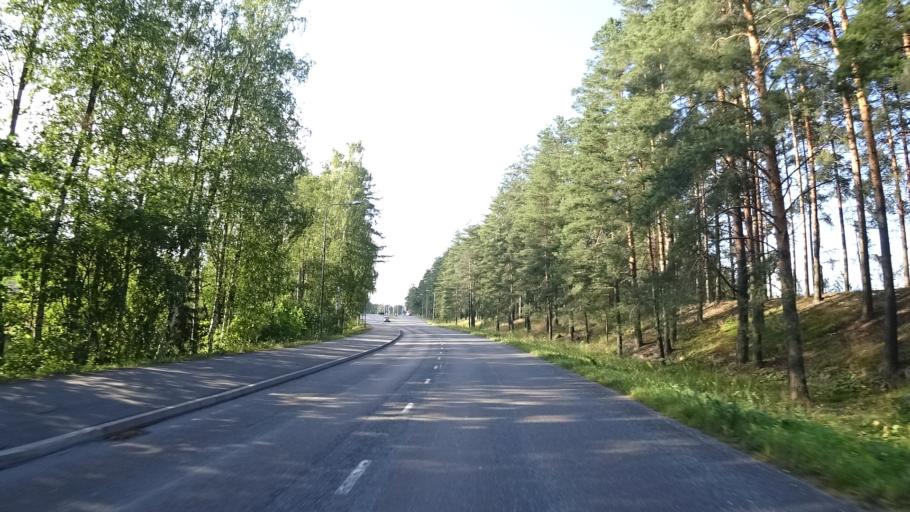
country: FI
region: South Karelia
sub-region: Imatra
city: Imatra
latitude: 61.1807
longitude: 28.7819
